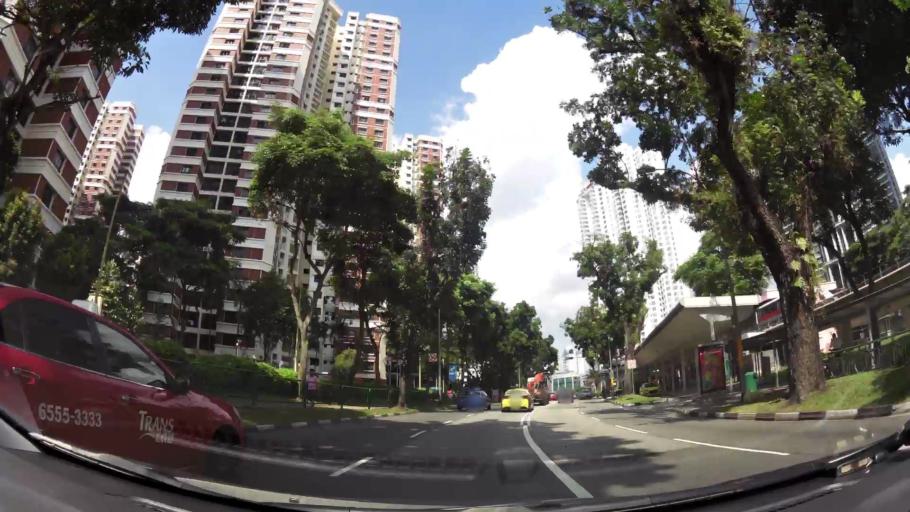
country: SG
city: Singapore
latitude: 1.2888
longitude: 103.8175
